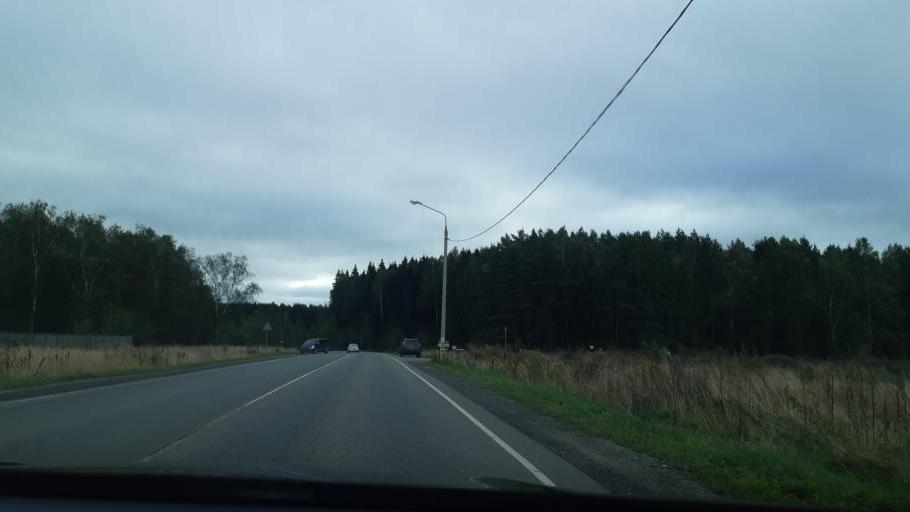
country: RU
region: Moskovskaya
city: Melikhovo
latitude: 55.1253
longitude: 37.6119
